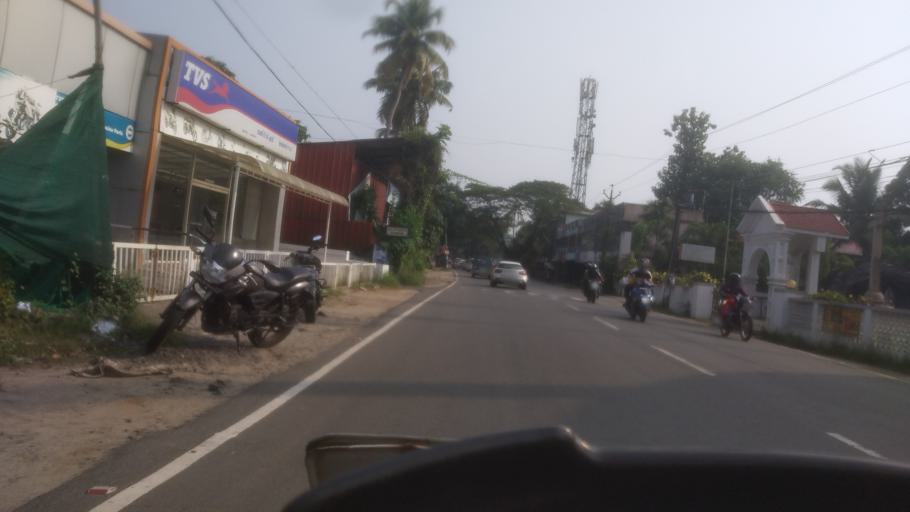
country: IN
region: Kerala
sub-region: Alappuzha
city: Arukutti
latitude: 9.9187
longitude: 76.3623
